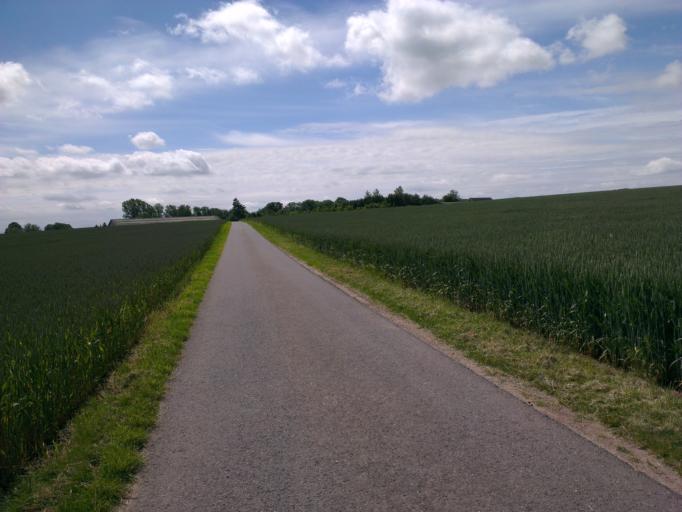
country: DK
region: Capital Region
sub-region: Frederikssund Kommune
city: Skibby
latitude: 55.7911
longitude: 11.9901
